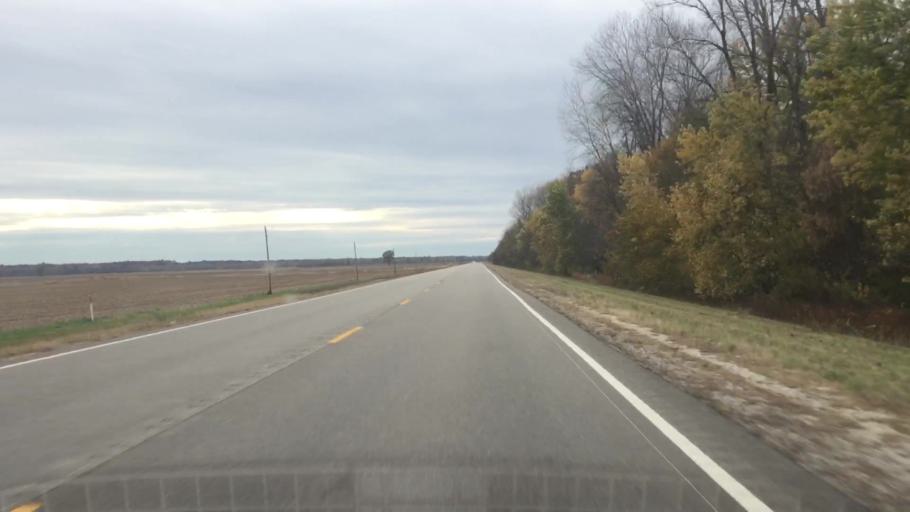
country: US
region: Missouri
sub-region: Callaway County
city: Holts Summit
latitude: 38.5819
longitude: -92.0684
